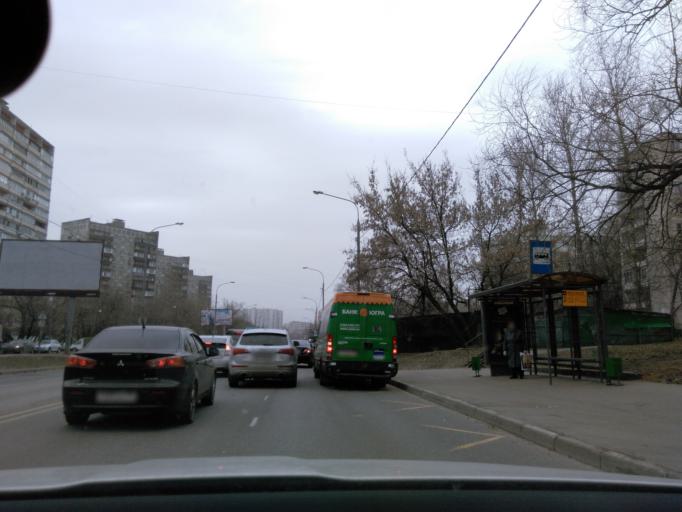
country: RU
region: Moscow
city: Novokhovrino
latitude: 55.8590
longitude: 37.5094
